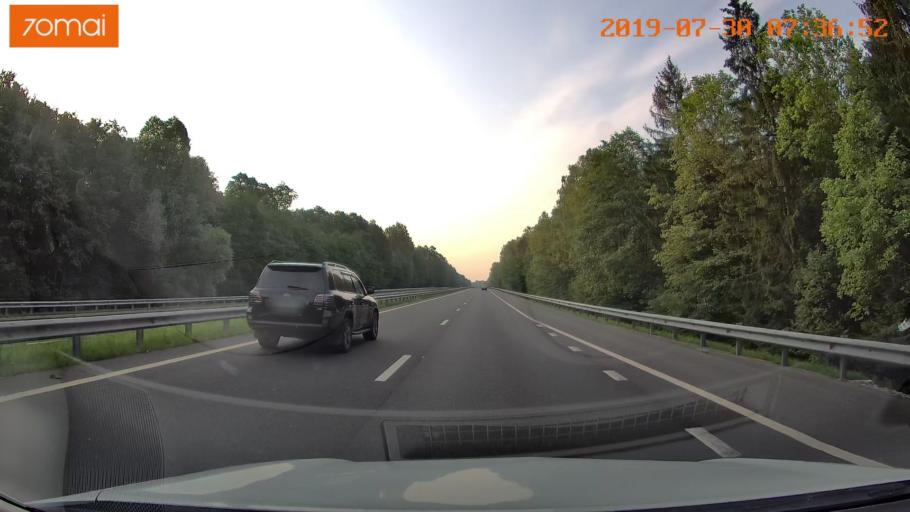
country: RU
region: Kaliningrad
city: Gvardeysk
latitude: 54.6607
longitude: 21.1340
